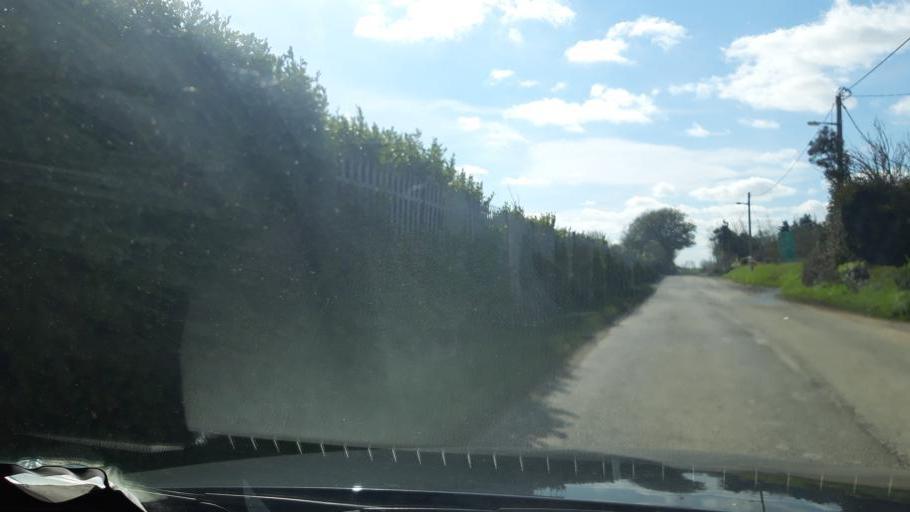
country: IE
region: Leinster
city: Malahide
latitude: 53.4302
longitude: -6.1680
